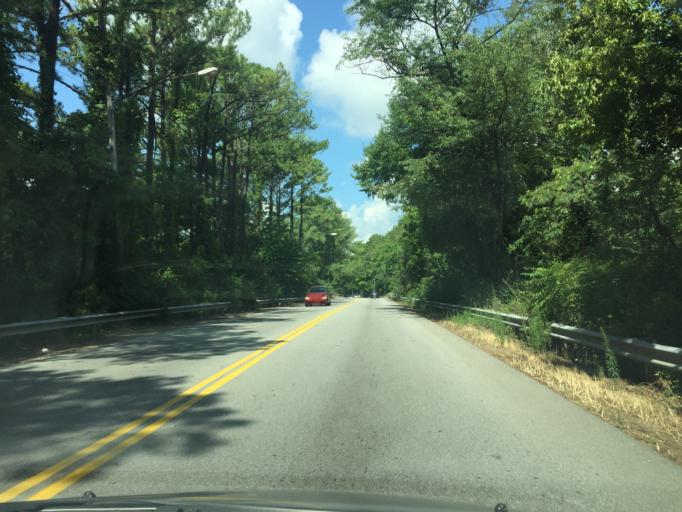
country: US
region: Tennessee
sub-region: Hamilton County
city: East Chattanooga
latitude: 35.0559
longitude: -85.2045
